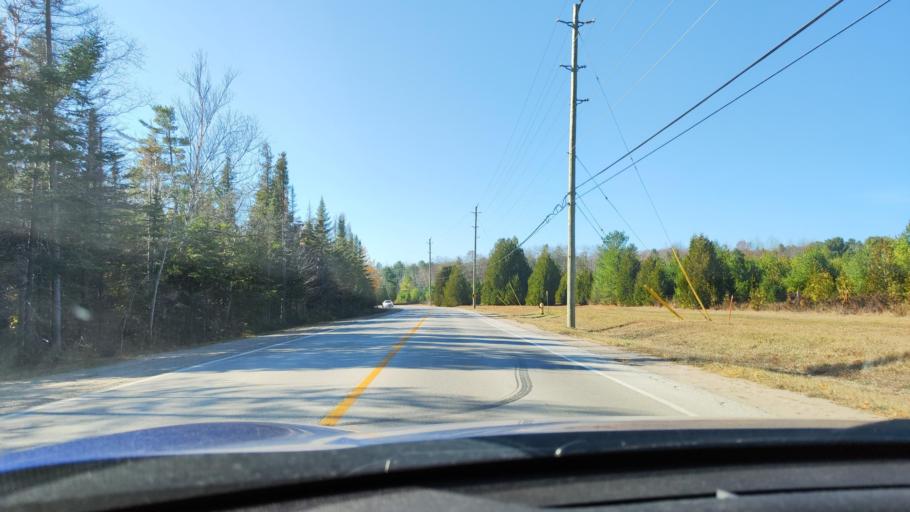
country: CA
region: Ontario
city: Wasaga Beach
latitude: 44.4991
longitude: -79.9958
